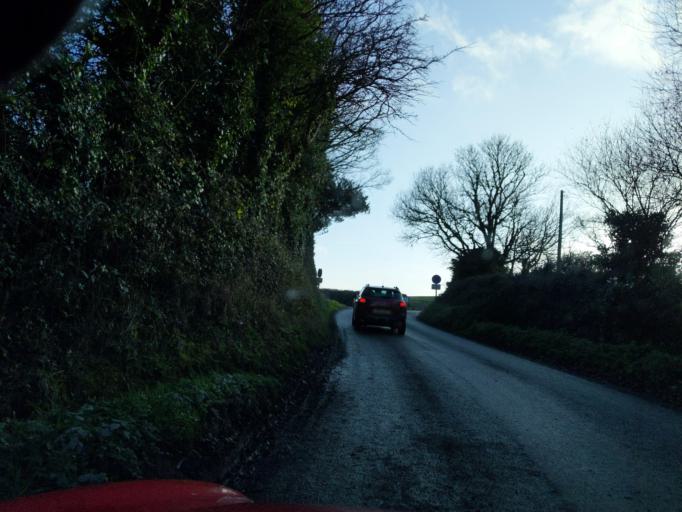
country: GB
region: England
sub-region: Cornwall
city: Fowey
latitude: 50.3358
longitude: -4.5908
